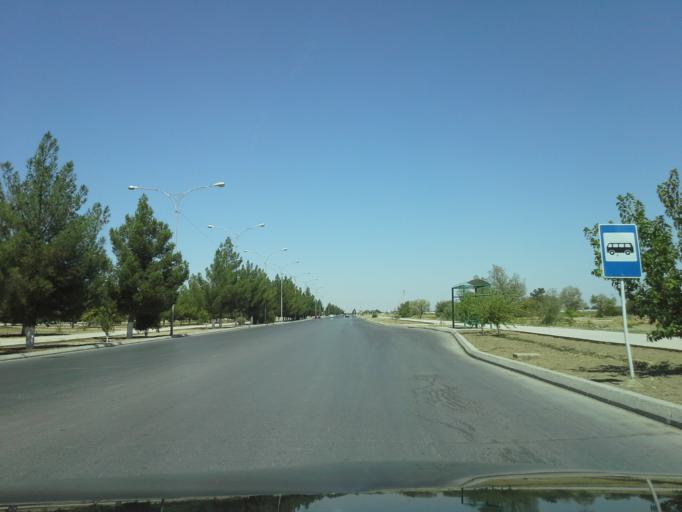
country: TM
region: Ahal
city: Ashgabat
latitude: 37.9945
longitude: 58.3235
